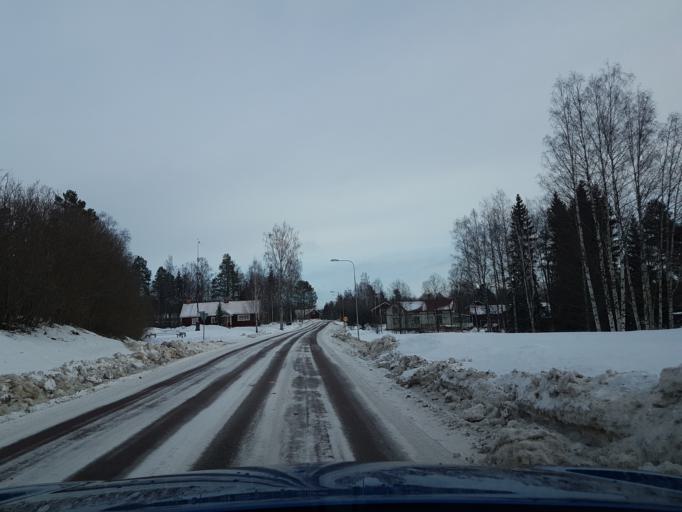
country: SE
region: Dalarna
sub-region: Leksand Municipality
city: Leksand
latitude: 60.7490
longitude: 15.0076
